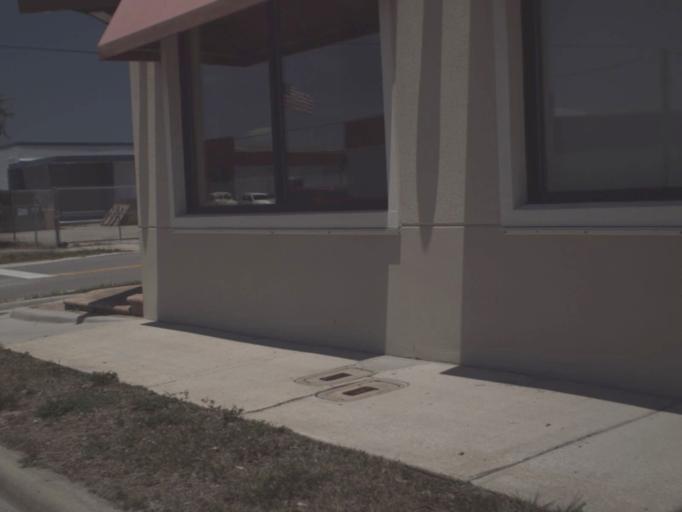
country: US
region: Florida
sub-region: Brevard County
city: Melbourne
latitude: 28.0668
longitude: -80.5990
